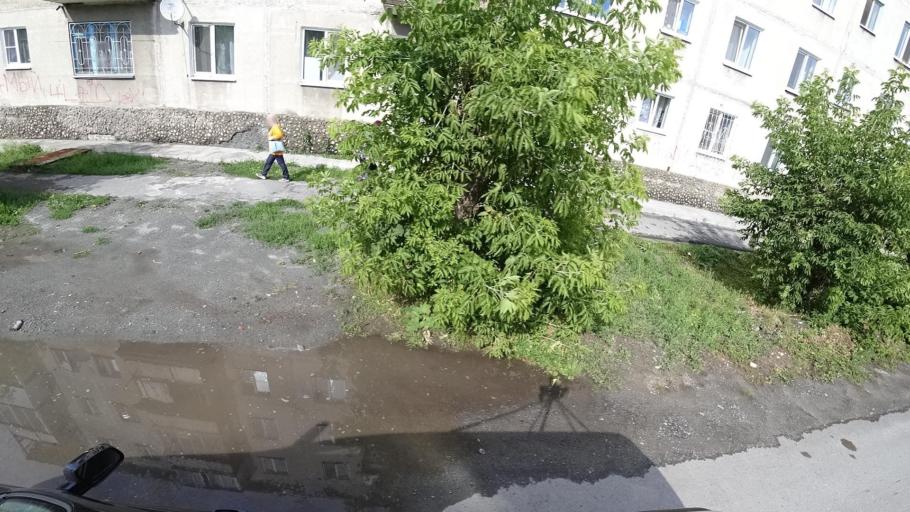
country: RU
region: Sverdlovsk
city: Kamyshlov
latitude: 56.8434
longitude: 62.7131
